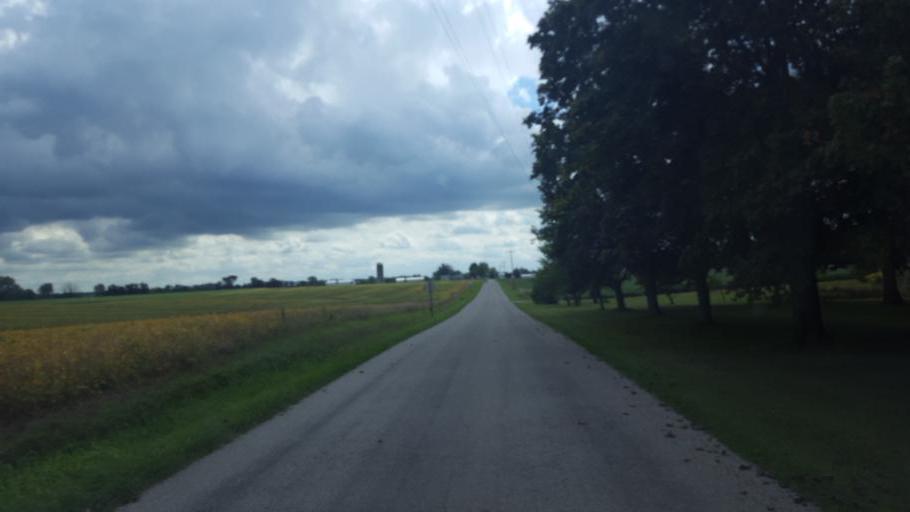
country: US
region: Ohio
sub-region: Huron County
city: Plymouth
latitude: 41.0677
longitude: -82.6433
